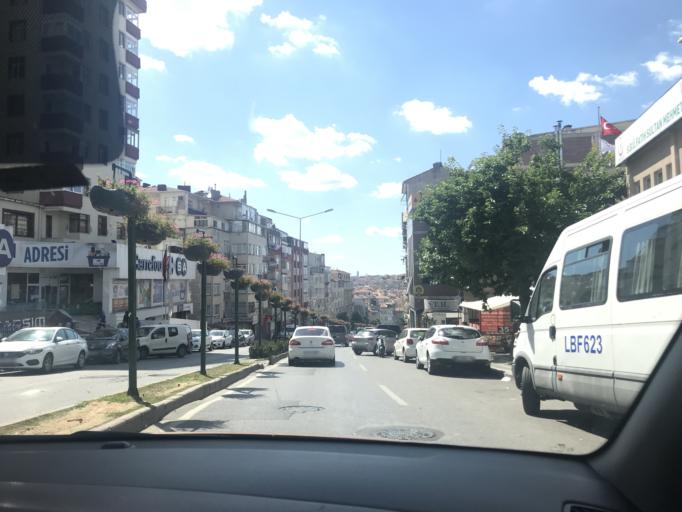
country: TR
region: Istanbul
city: UEskuedar
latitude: 41.0167
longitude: 29.0243
